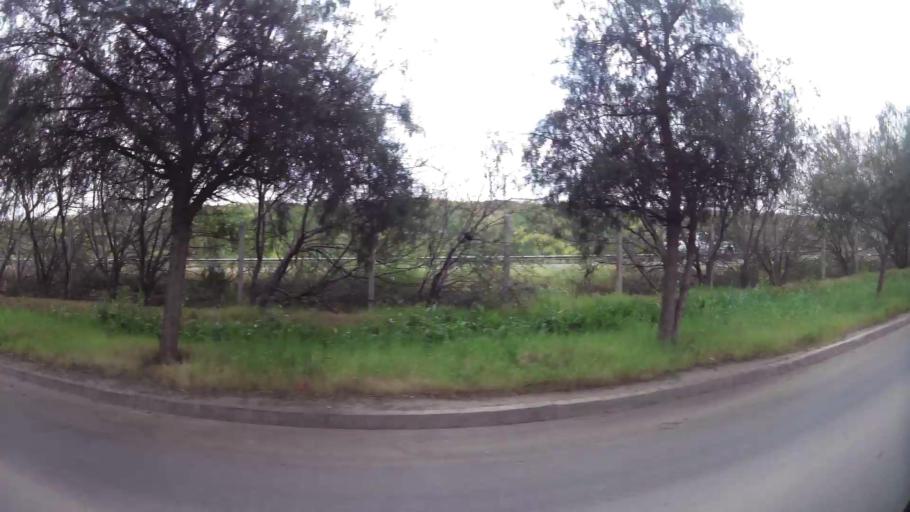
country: CL
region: Santiago Metropolitan
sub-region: Provincia de Chacabuco
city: Chicureo Abajo
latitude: -33.2036
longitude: -70.6639
